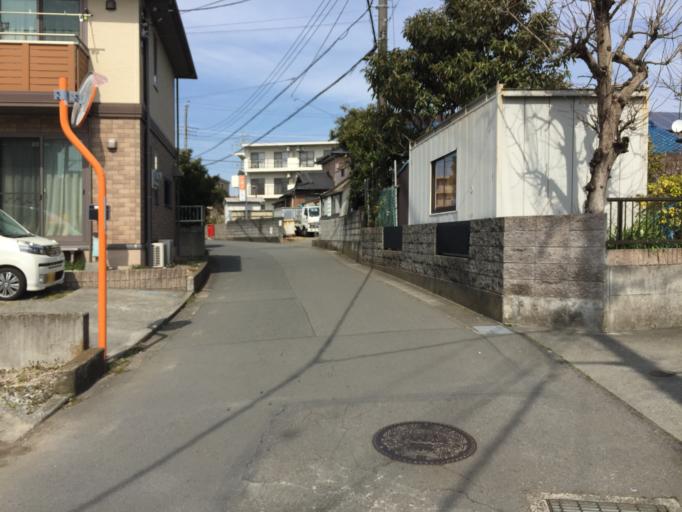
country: JP
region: Shizuoka
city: Mishima
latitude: 35.1674
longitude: 138.9141
